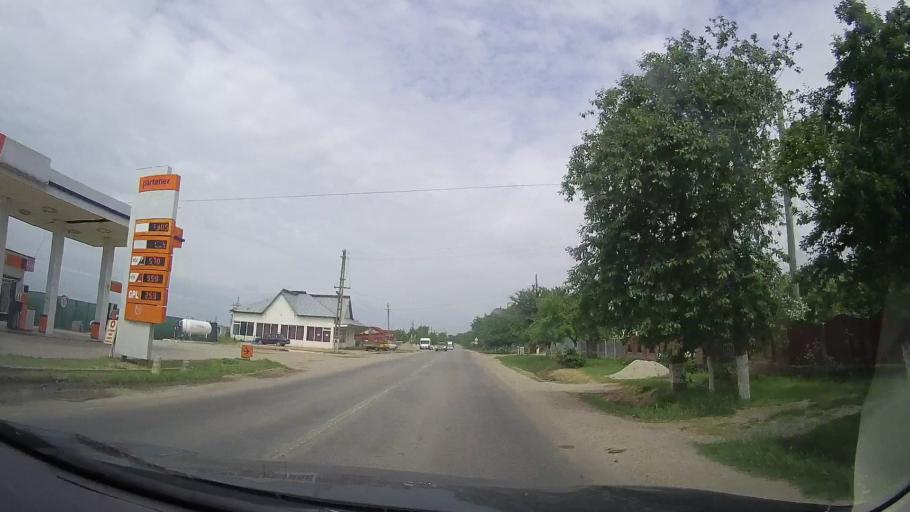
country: RO
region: Olt
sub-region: Comuna Daneasa
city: Daneasa
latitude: 44.1332
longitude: 24.5708
